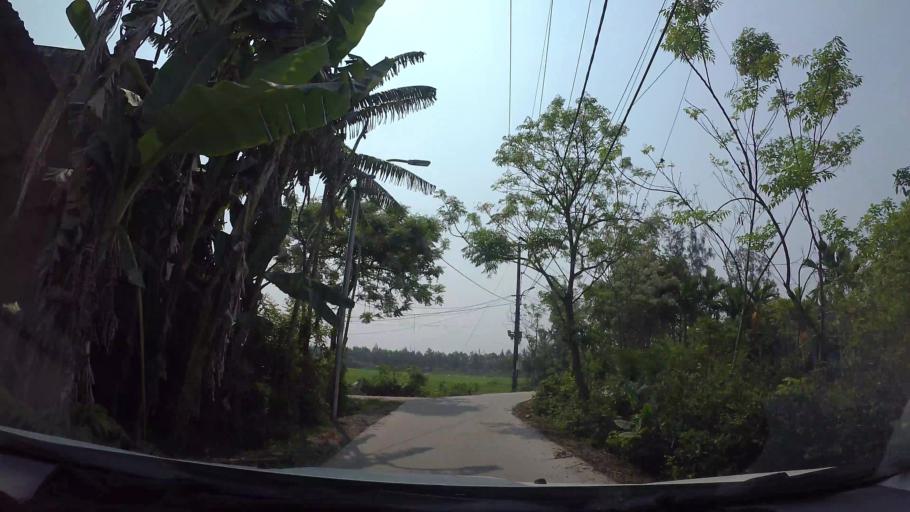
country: VN
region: Da Nang
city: Cam Le
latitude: 15.9759
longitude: 108.2267
